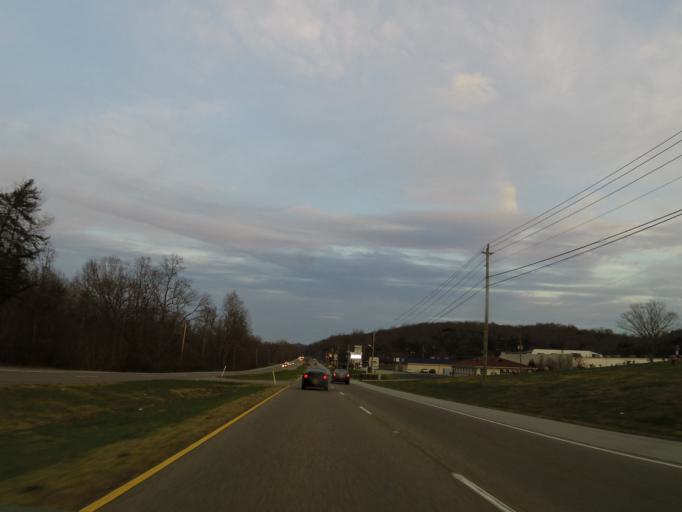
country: US
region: Tennessee
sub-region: Roane County
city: Rockwood
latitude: 35.8877
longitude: -84.6468
